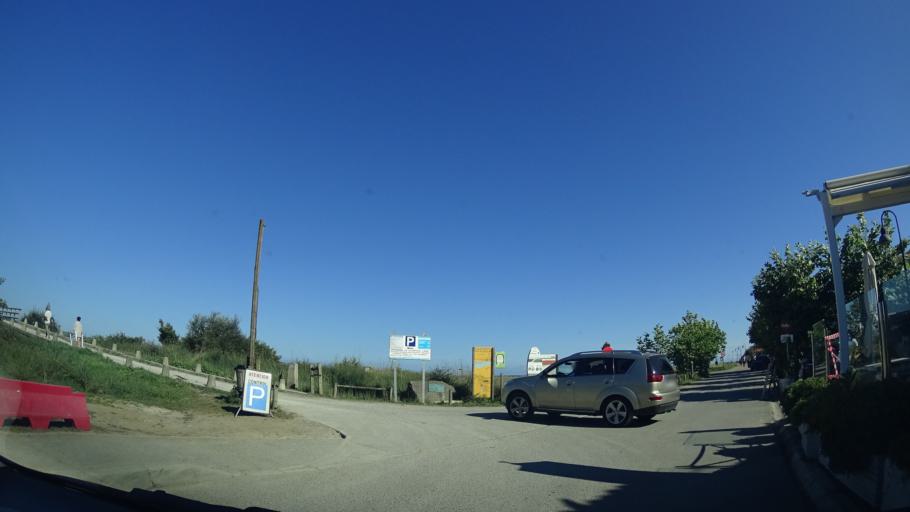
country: ES
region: Asturias
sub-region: Province of Asturias
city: Ribadesella
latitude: 43.4794
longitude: -5.1344
